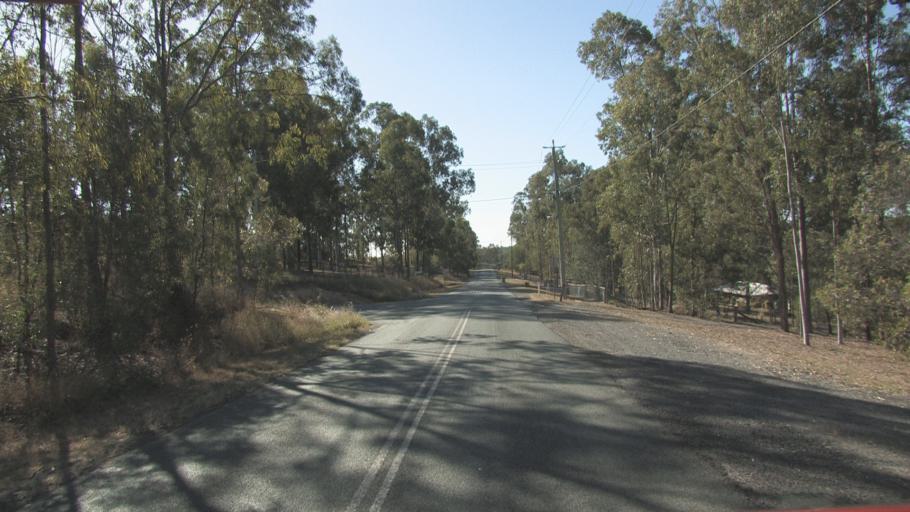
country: AU
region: Queensland
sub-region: Logan
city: Cedar Vale
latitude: -27.8589
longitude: 153.0372
